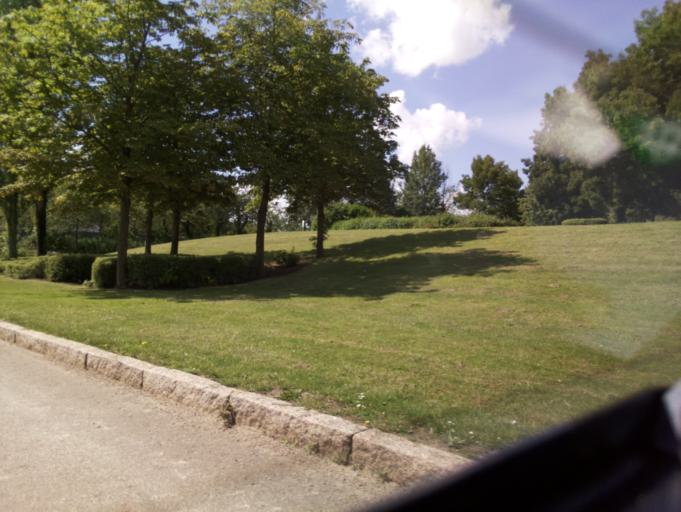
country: GB
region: England
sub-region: Milton Keynes
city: Milton Keynes
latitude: 52.0478
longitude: -0.7358
